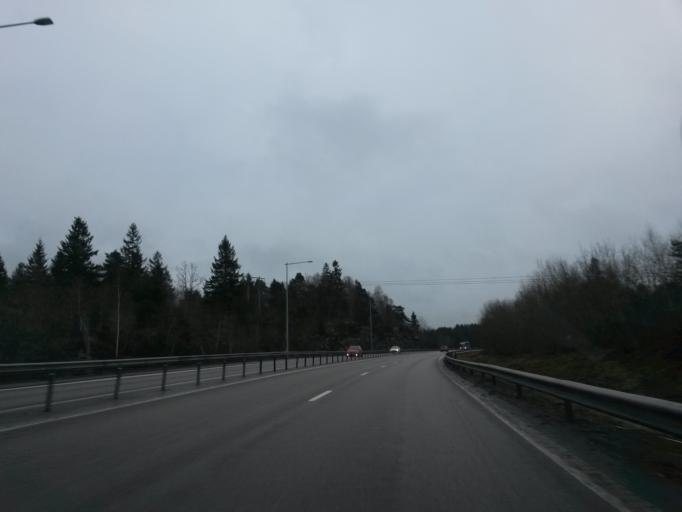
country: SE
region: Vaestra Goetaland
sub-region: Uddevalla Kommun
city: Uddevalla
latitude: 58.3470
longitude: 11.9865
